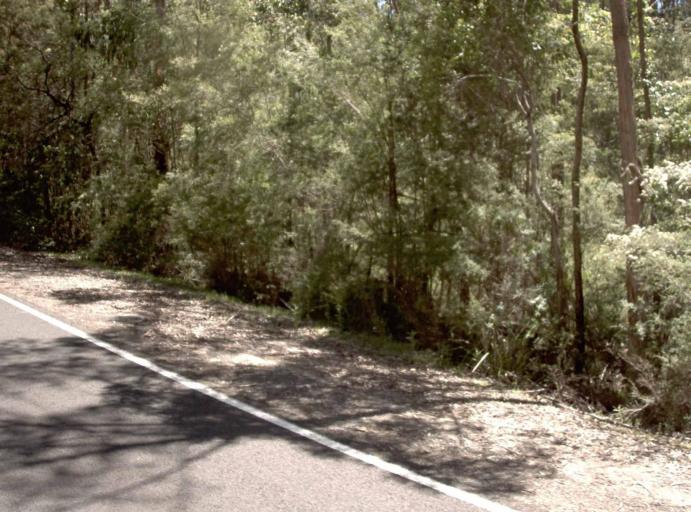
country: AU
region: Victoria
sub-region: East Gippsland
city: Lakes Entrance
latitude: -37.3670
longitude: 148.2183
